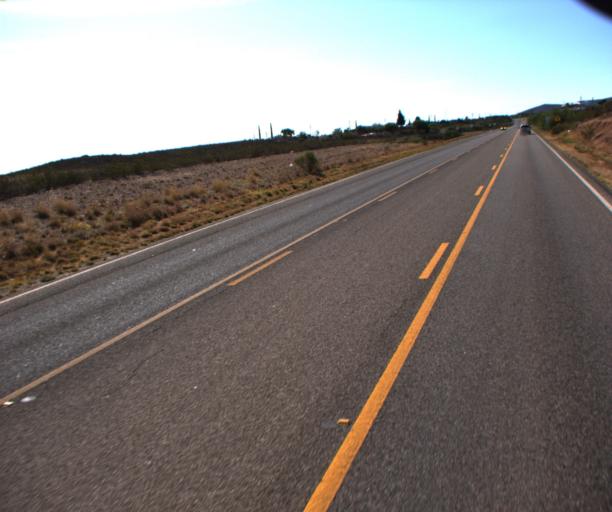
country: US
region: Arizona
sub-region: Cochise County
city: Tombstone
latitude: 31.7255
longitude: -110.0754
